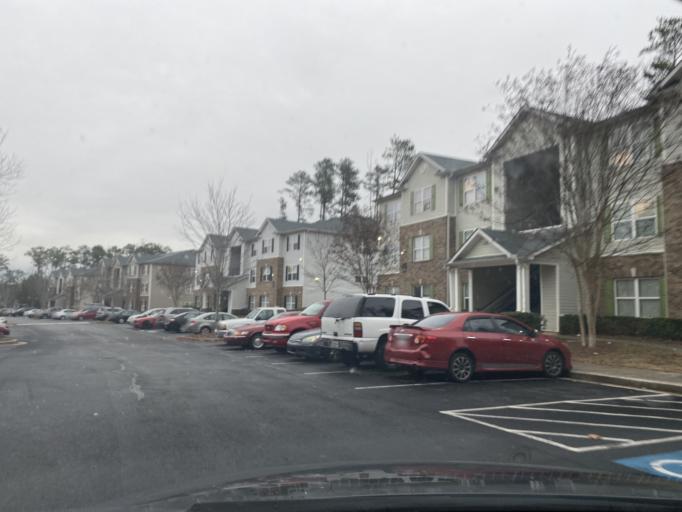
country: US
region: Georgia
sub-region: DeKalb County
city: Pine Mountain
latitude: 33.6972
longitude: -84.1538
